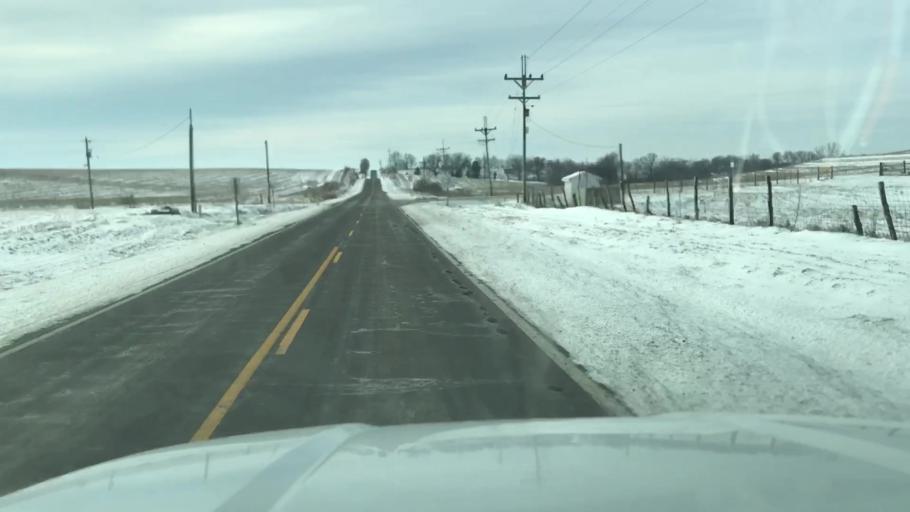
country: US
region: Missouri
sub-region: Holt County
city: Oregon
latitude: 40.0802
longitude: -95.1355
